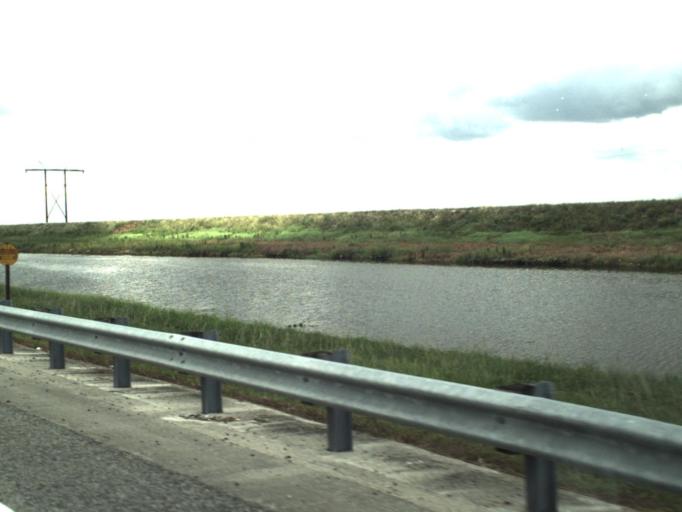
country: US
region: Florida
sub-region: Broward County
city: Weston
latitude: 26.1297
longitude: -80.3750
